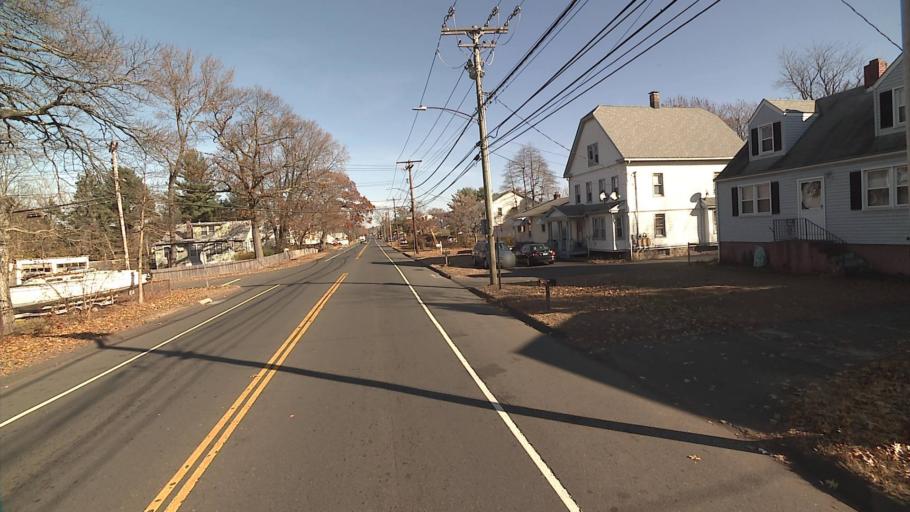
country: US
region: Connecticut
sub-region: New Haven County
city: East Haven
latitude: 41.3311
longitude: -72.8743
